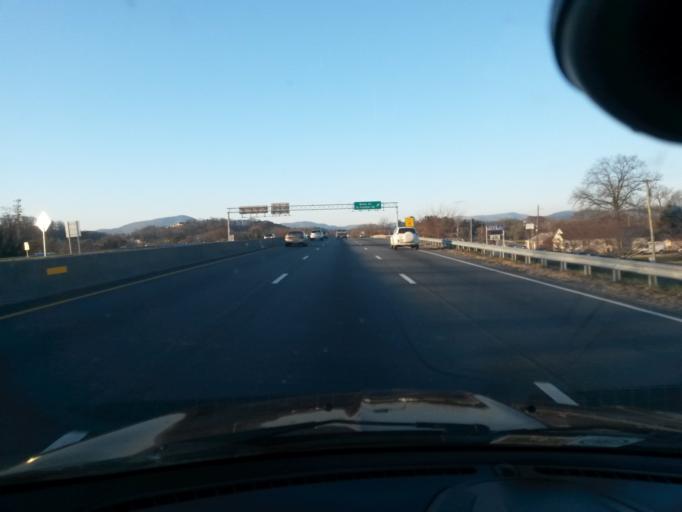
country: US
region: Virginia
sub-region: City of Roanoke
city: Roanoke
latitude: 37.2532
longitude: -79.9561
